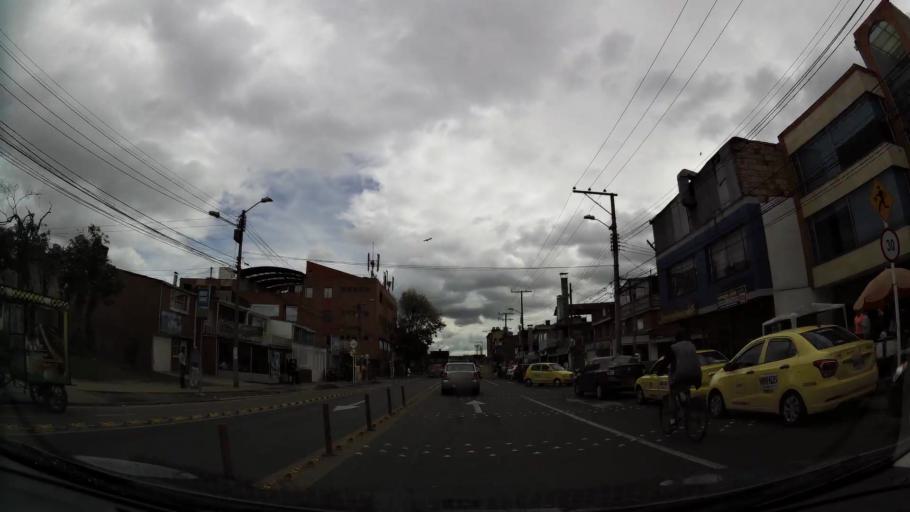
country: CO
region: Bogota D.C.
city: Barrio San Luis
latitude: 4.6917
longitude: -74.0979
